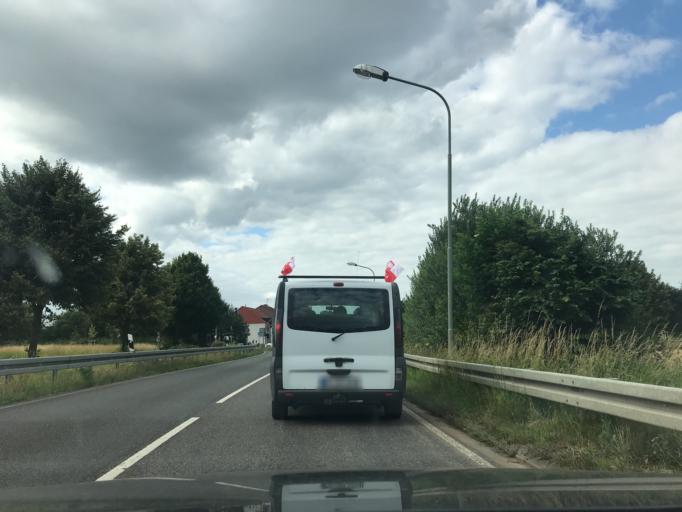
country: DE
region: North Rhine-Westphalia
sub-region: Regierungsbezirk Dusseldorf
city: Neuss
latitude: 51.1389
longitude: 6.7223
